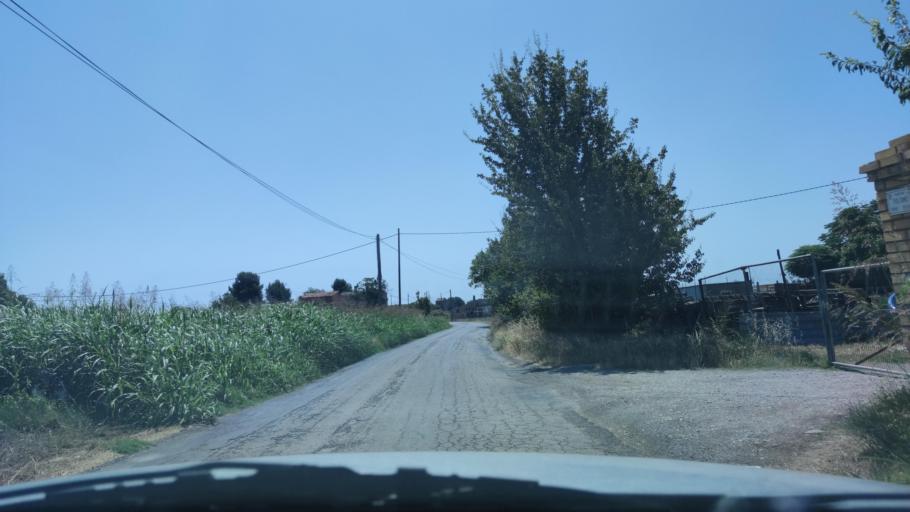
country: ES
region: Catalonia
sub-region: Provincia de Lleida
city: Alpicat
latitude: 41.6515
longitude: 0.5784
